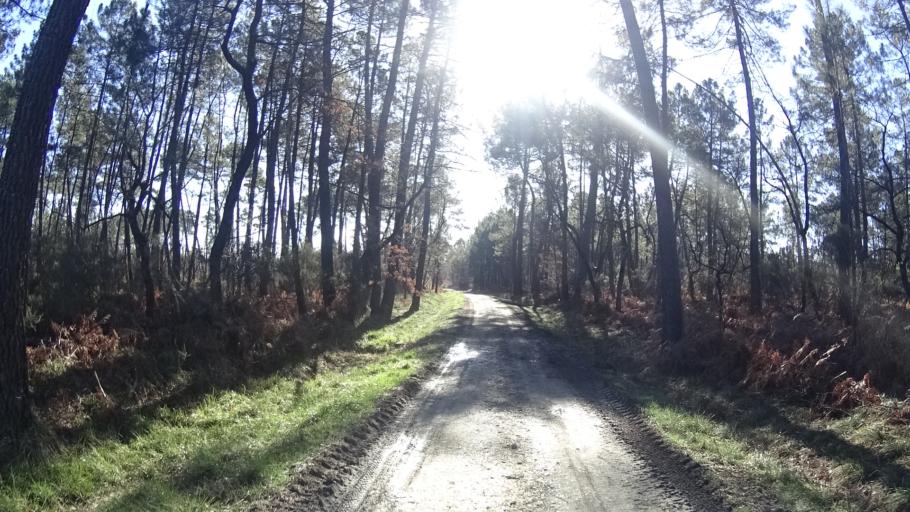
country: FR
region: Aquitaine
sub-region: Departement de la Dordogne
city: La Roche-Chalais
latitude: 45.1687
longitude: 0.0384
